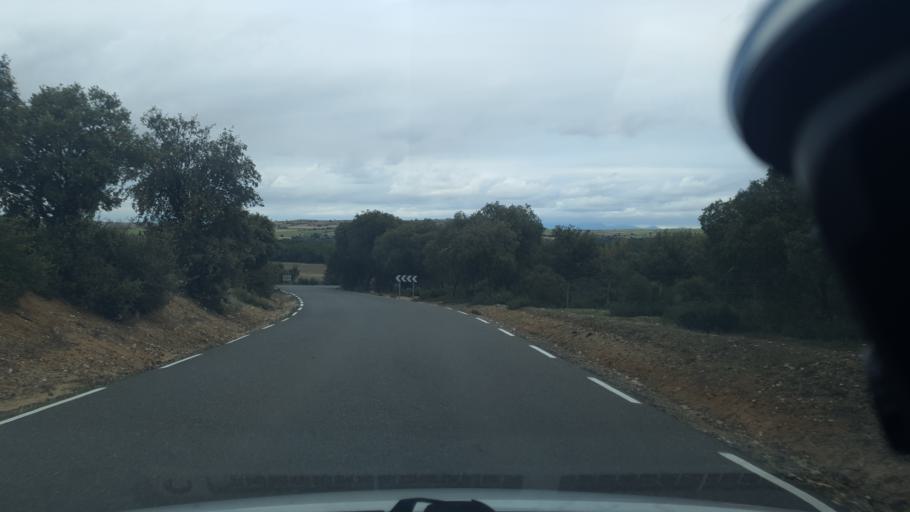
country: ES
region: Castille and Leon
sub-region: Provincia de Avila
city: Gotarrendura
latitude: 40.8257
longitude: -4.7068
